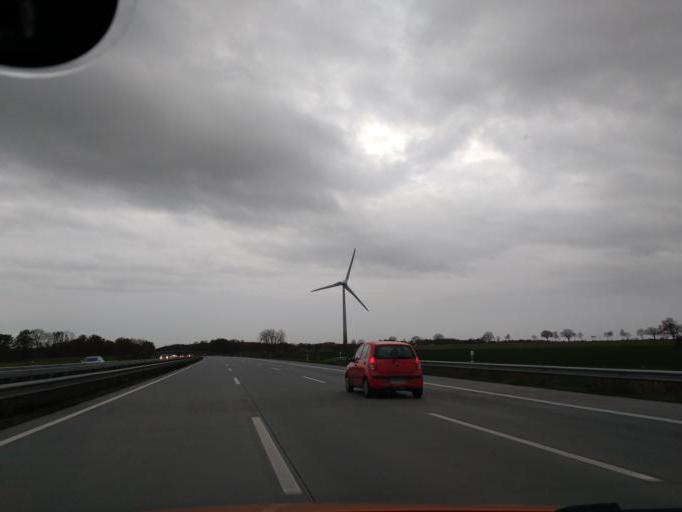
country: DE
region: Lower Saxony
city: Reessum
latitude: 53.1442
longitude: 9.2249
